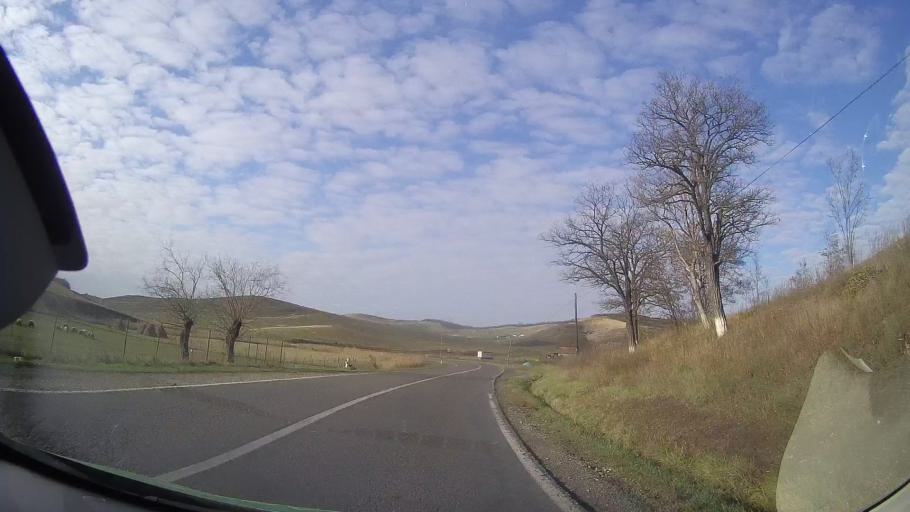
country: RO
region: Cluj
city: Jucu Herghelia
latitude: 46.8119
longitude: 23.8174
